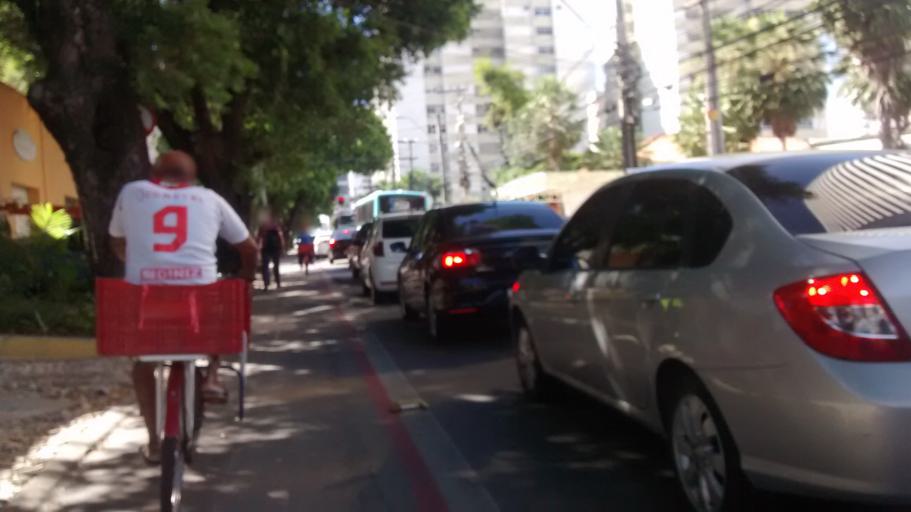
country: BR
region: Ceara
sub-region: Fortaleza
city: Fortaleza
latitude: -3.7340
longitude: -38.5050
